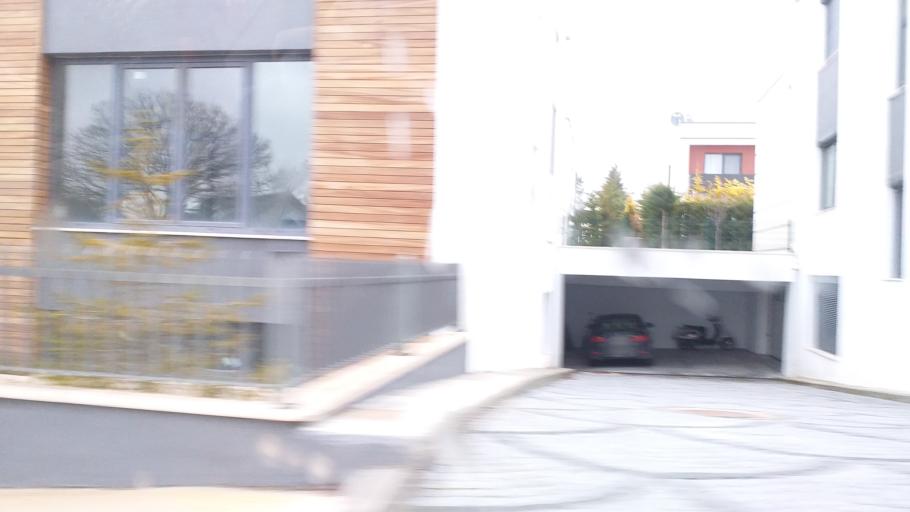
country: TR
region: Ankara
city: Batikent
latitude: 39.8762
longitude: 32.7144
